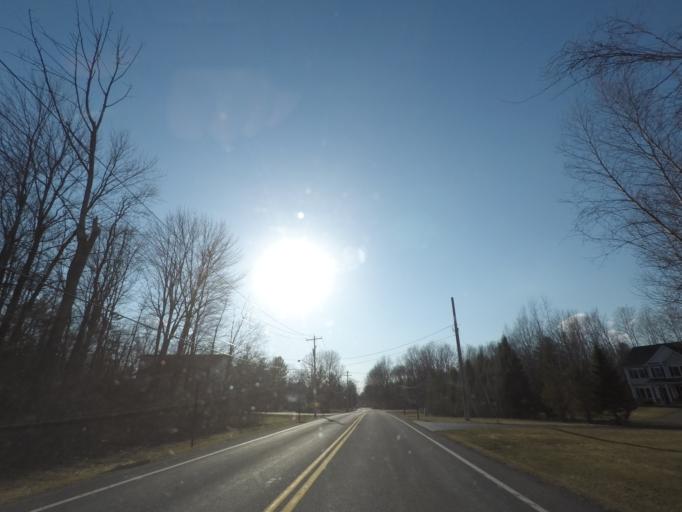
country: US
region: New York
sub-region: Schenectady County
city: Niskayuna
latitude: 42.8329
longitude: -73.7925
